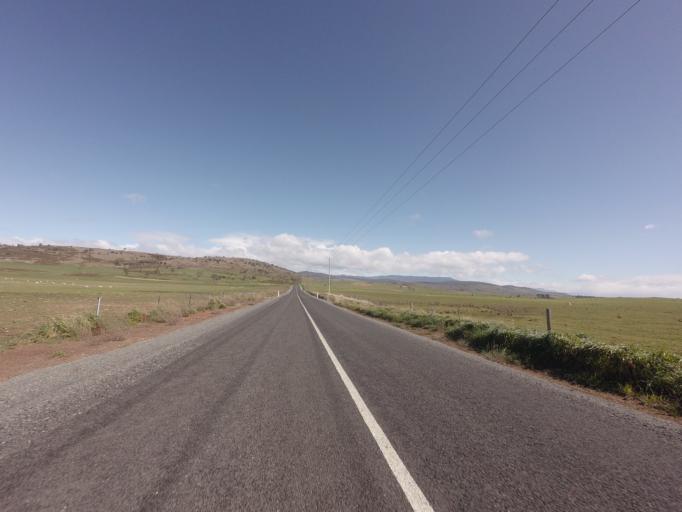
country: AU
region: Tasmania
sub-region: Northern Midlands
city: Evandale
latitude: -41.9098
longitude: 147.3830
